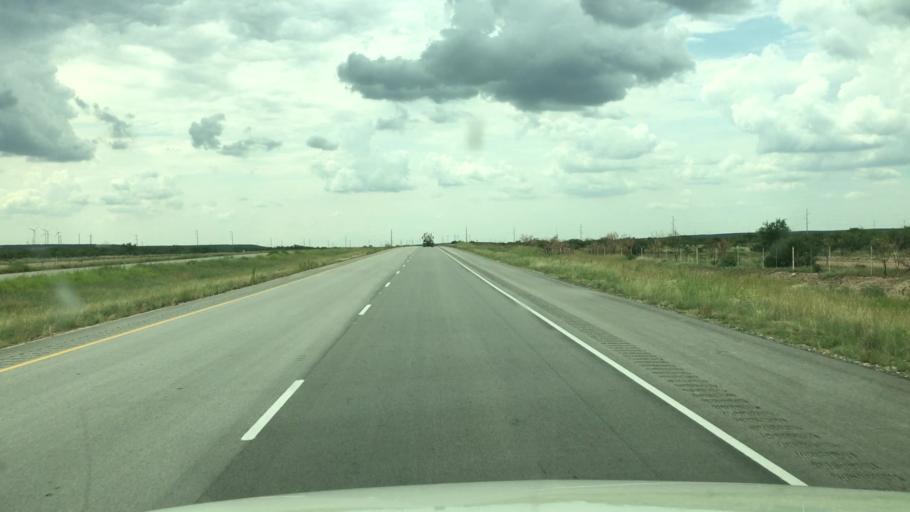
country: US
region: Texas
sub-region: Sterling County
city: Sterling City
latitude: 31.9558
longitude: -101.1967
